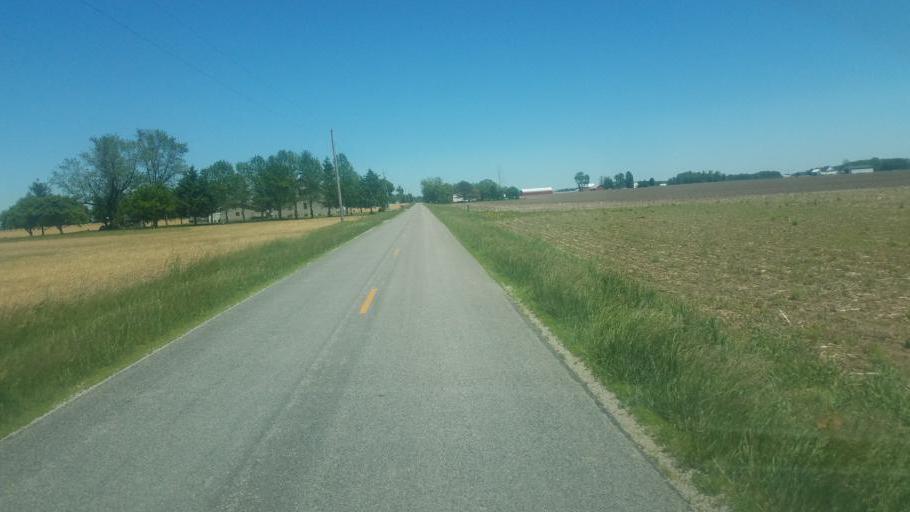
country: US
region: Ohio
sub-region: Shelby County
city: Sidney
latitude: 40.2089
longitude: -84.0863
